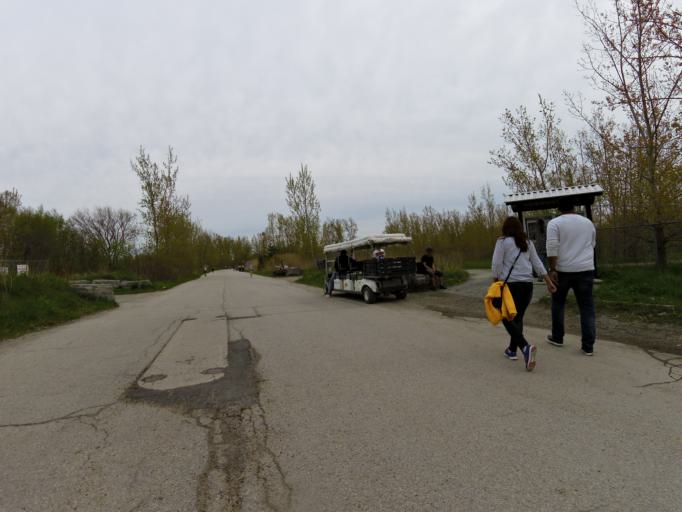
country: CA
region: Ontario
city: Toronto
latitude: 43.6518
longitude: -79.3224
